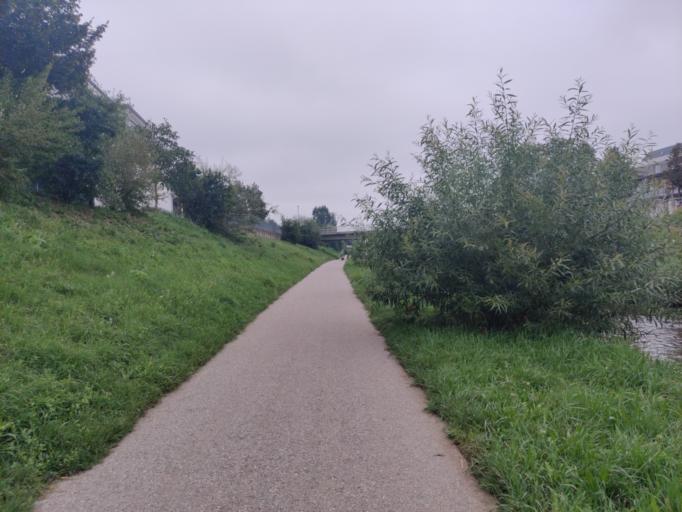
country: AT
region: Lower Austria
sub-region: Krems an der Donau Stadt
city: Krems an der Donau
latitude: 48.4106
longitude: 15.6151
